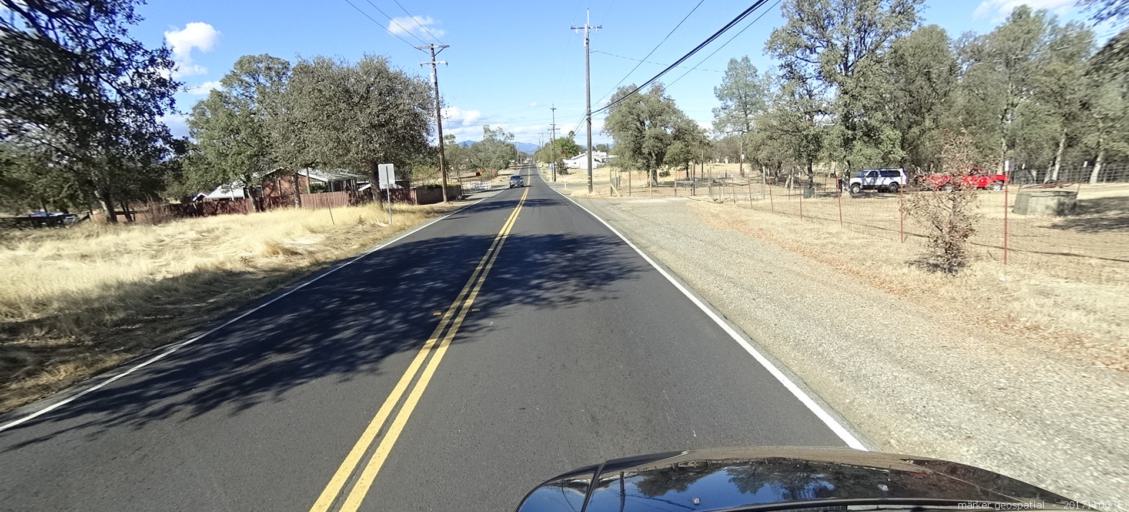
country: US
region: California
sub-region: Shasta County
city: Palo Cedro
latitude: 40.5702
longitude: -122.2998
